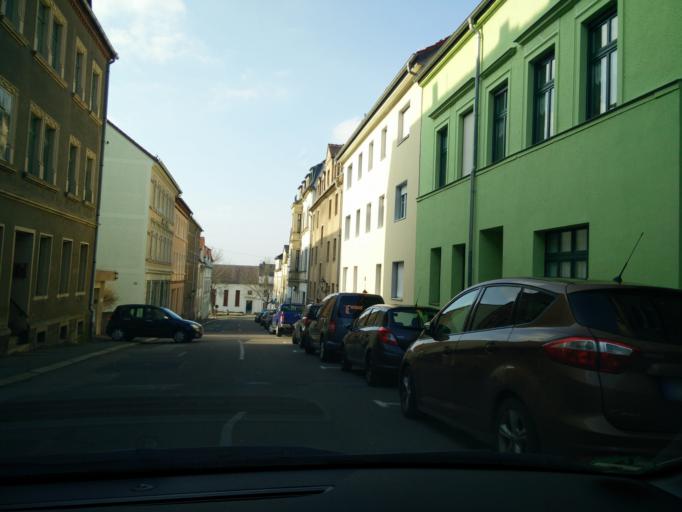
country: DE
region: Saxony
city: Colditz
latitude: 51.1272
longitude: 12.8072
